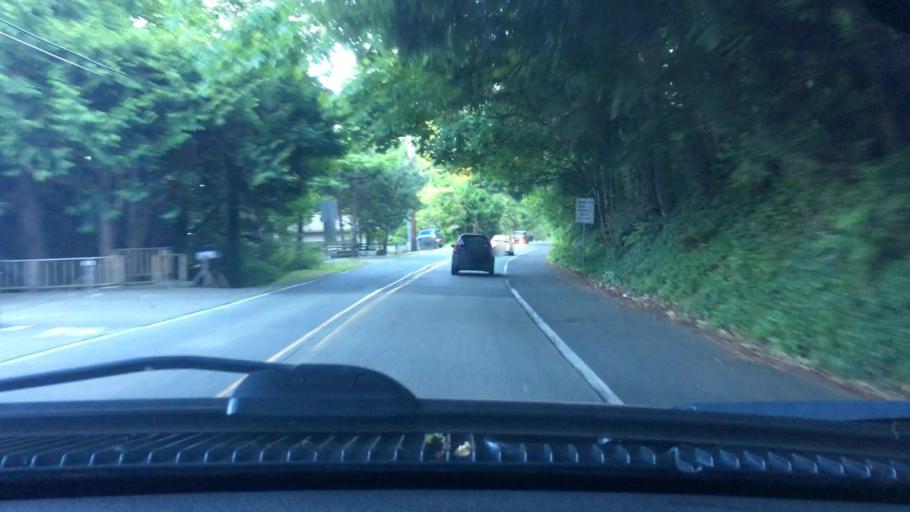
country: US
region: Washington
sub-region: King County
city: Sammamish
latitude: 47.6277
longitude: -122.0882
